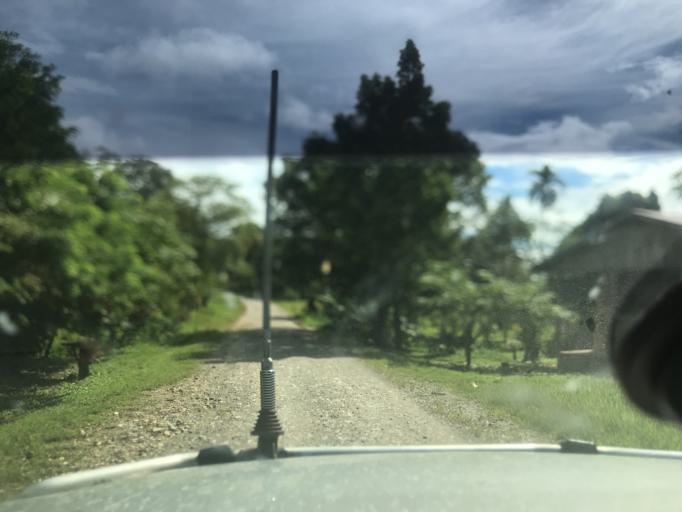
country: SB
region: Malaita
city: Auki
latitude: -8.3814
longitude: 160.7021
